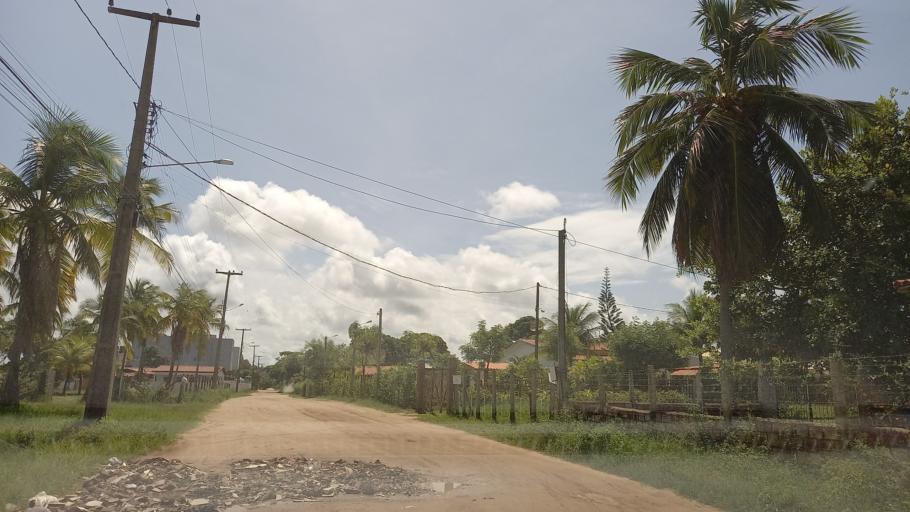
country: BR
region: Pernambuco
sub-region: Sao Jose Da Coroa Grande
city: Sao Jose da Coroa Grande
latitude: -8.9244
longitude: -35.1615
